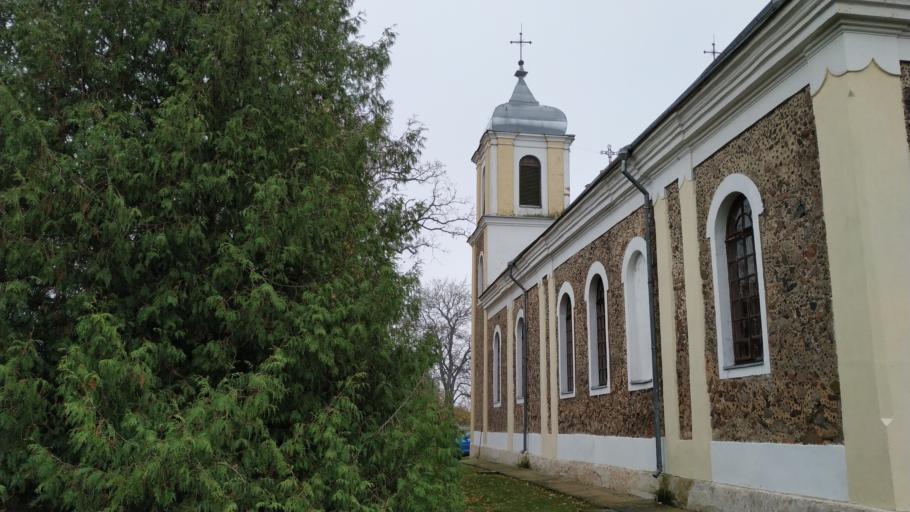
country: LT
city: Skaidiskes
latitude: 54.6157
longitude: 25.5050
